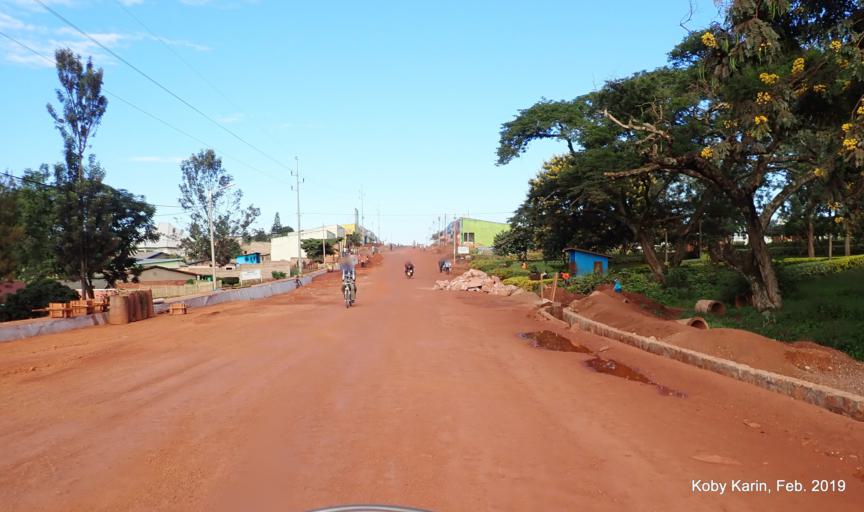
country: RW
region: Eastern Province
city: Kibungo
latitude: -2.2746
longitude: 30.6732
